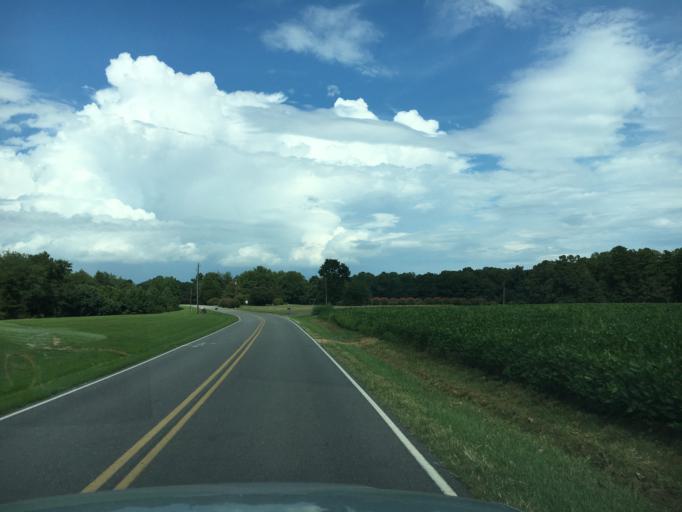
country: US
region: North Carolina
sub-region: Catawba County
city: Claremont
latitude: 35.6383
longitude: -81.1188
